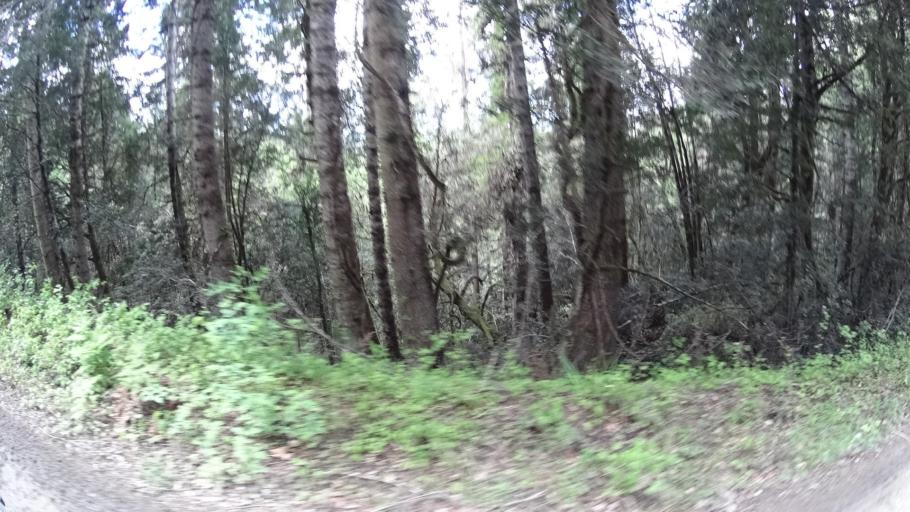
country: US
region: California
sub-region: Humboldt County
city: Blue Lake
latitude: 40.7928
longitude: -123.8776
